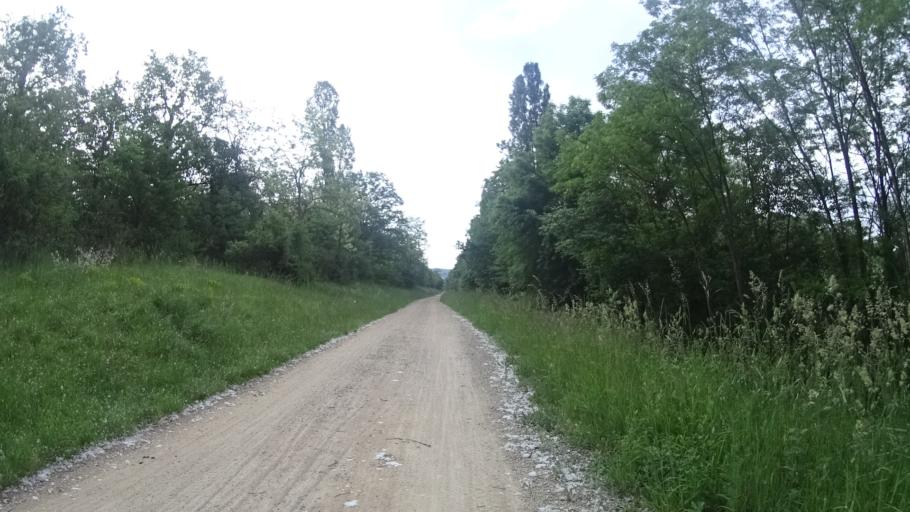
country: DE
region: Baden-Wuerttemberg
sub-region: Freiburg Region
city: Bad Bellingen
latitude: 47.7536
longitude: 7.5419
